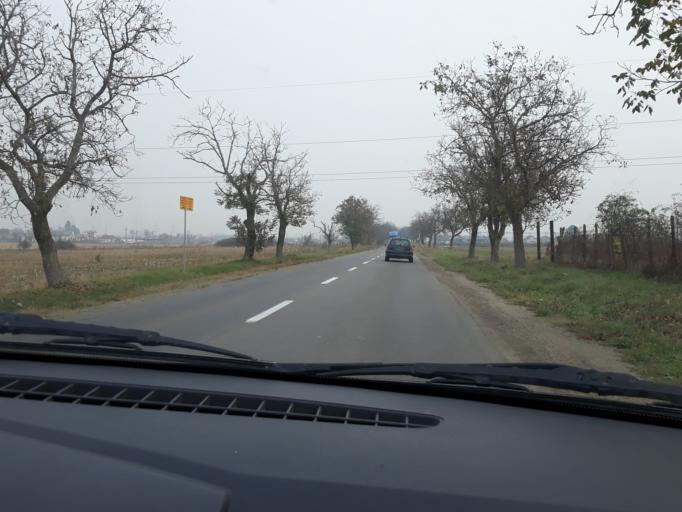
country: RO
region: Bihor
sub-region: Comuna Santandrei
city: Santandrei
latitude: 47.0537
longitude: 21.8716
